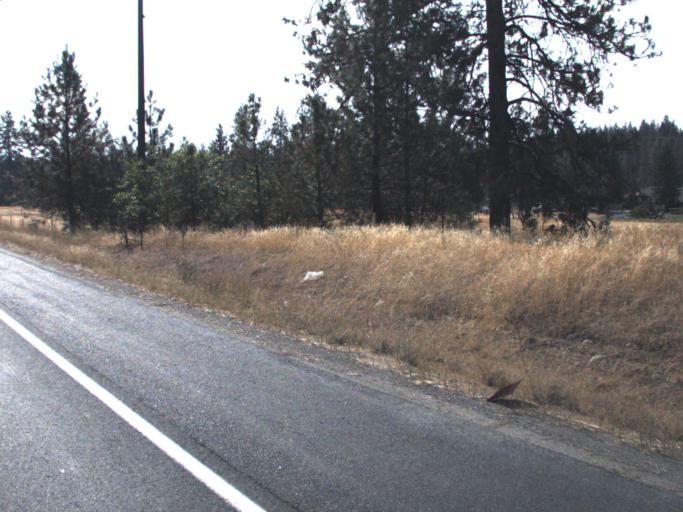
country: US
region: Washington
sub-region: Spokane County
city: Fairwood
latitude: 47.7604
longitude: -117.5341
